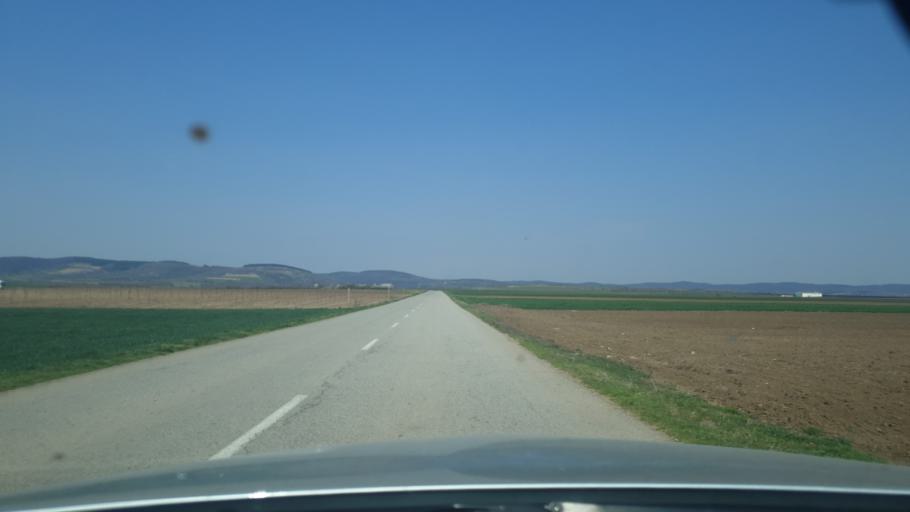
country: RS
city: Vrdnik
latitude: 45.0786
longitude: 19.7698
